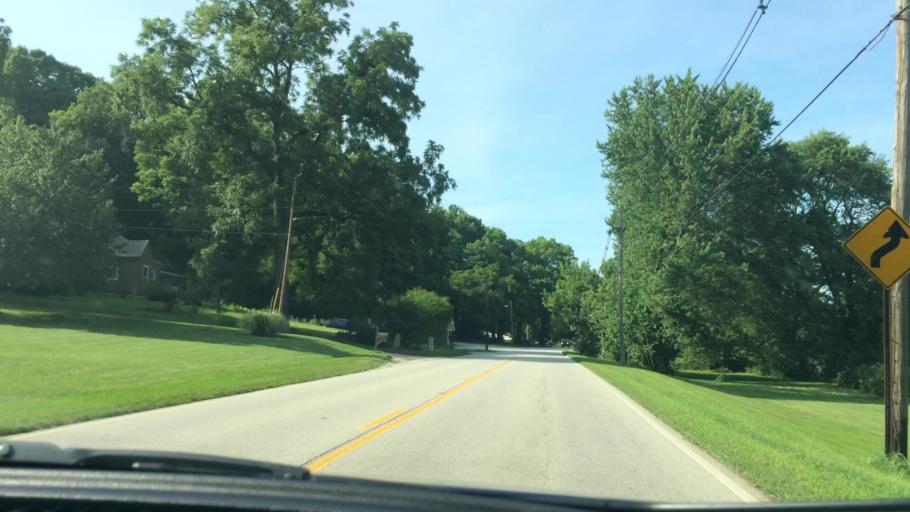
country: US
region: Indiana
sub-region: Tippecanoe County
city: West Lafayette
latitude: 40.4424
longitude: -86.8969
